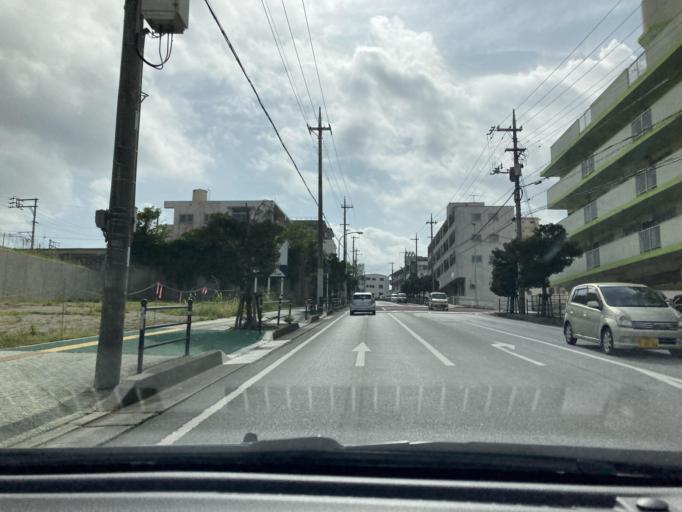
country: JP
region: Okinawa
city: Ginowan
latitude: 26.2626
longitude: 127.7500
